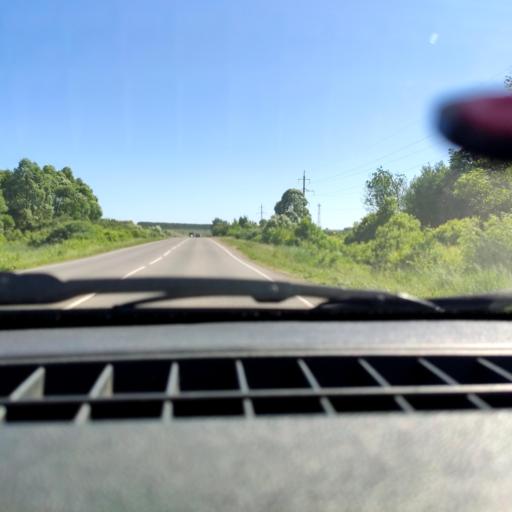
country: RU
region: Bashkortostan
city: Iglino
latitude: 54.8874
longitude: 56.4709
